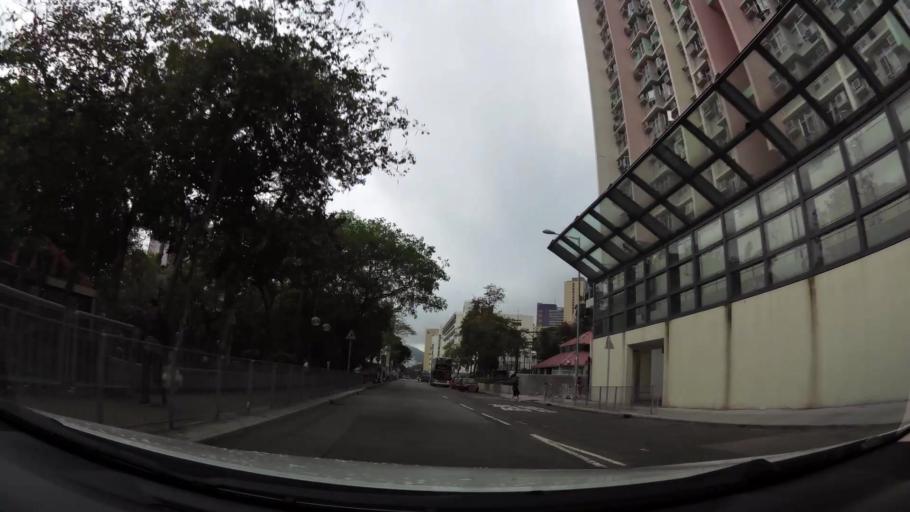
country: HK
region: Tsuen Wan
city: Tsuen Wan
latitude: 22.3616
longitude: 114.1261
